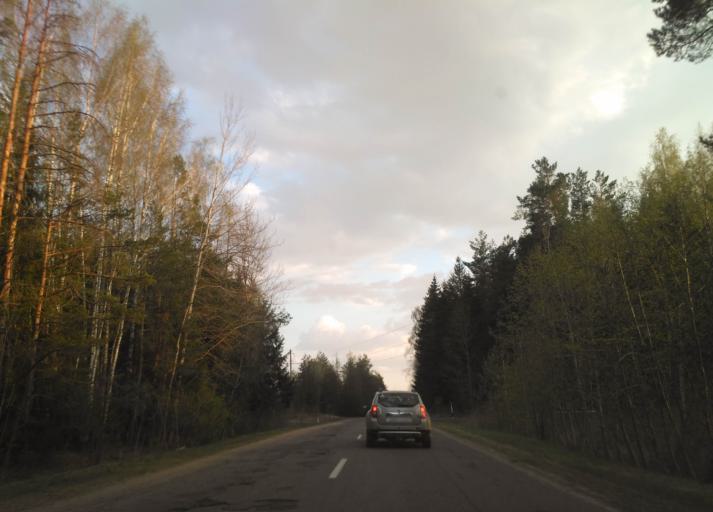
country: BY
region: Minsk
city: Loshnitsa
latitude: 54.4518
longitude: 28.6413
